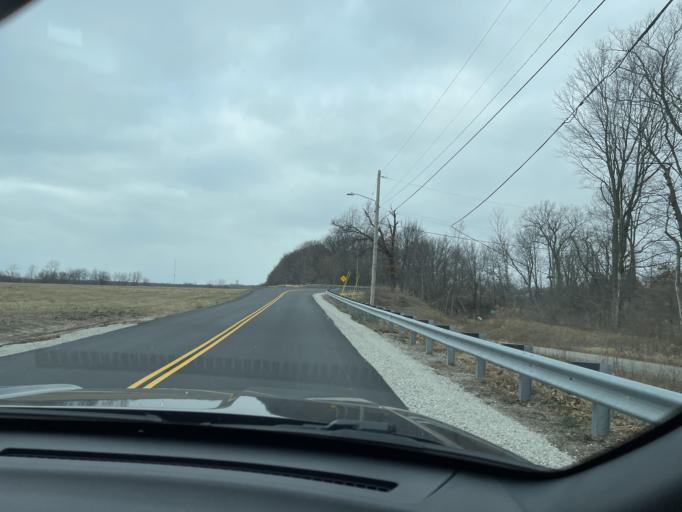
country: US
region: Illinois
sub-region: Sangamon County
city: Rochester
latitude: 39.7732
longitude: -89.5793
